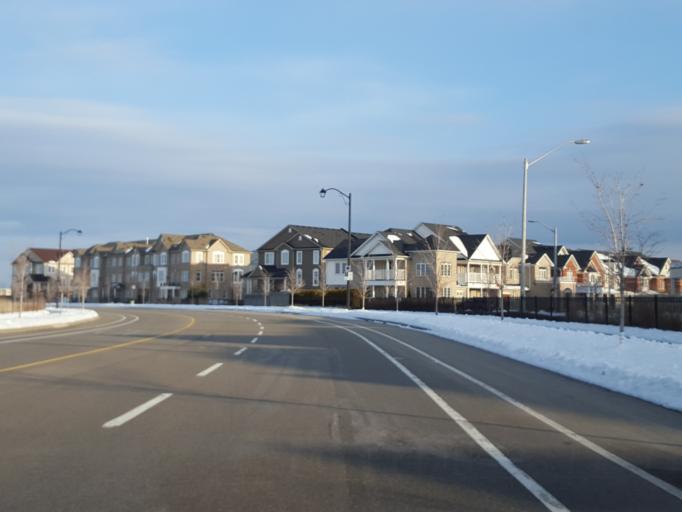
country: CA
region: Ontario
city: Burlington
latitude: 43.4109
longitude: -79.8200
